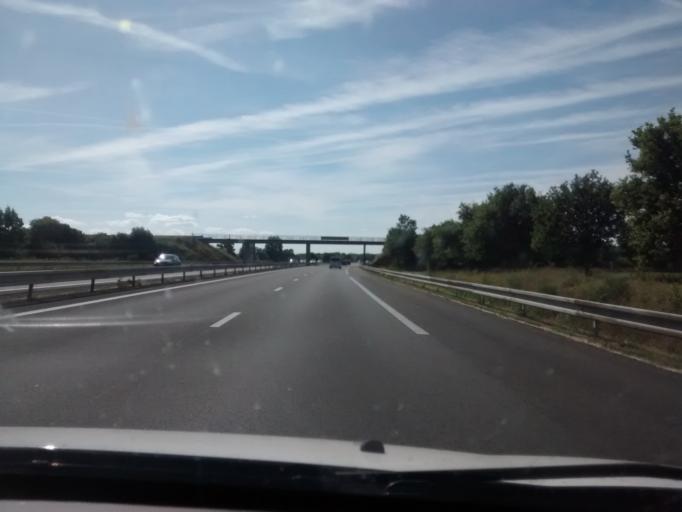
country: FR
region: Pays de la Loire
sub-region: Departement de la Sarthe
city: Brulon
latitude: 48.0074
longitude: -0.2835
